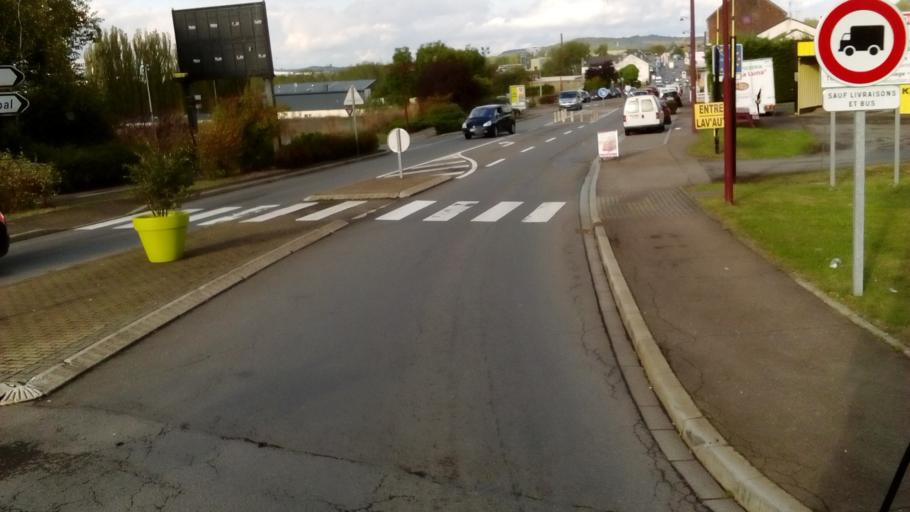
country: FR
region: Lorraine
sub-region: Departement de Meurthe-et-Moselle
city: Longlaville
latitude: 49.5388
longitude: 5.8109
